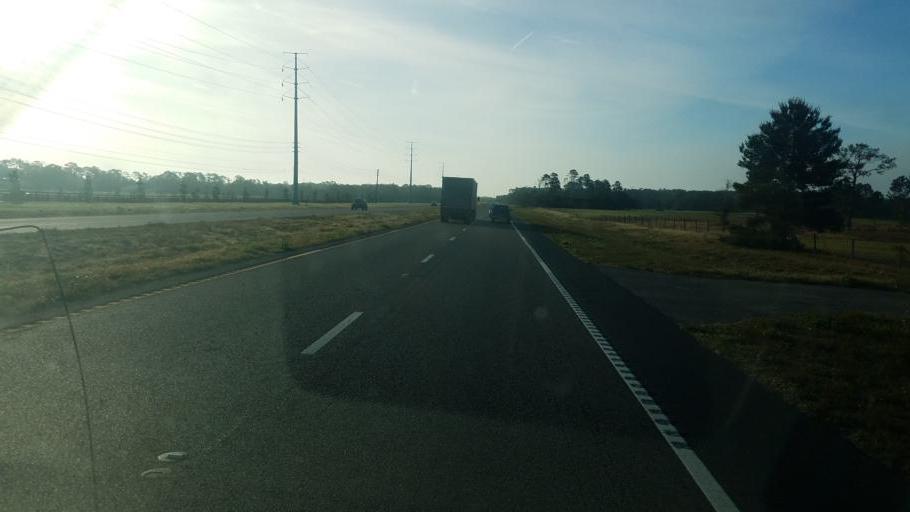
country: US
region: Florida
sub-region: Osceola County
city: Saint Cloud
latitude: 28.2113
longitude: -81.1738
